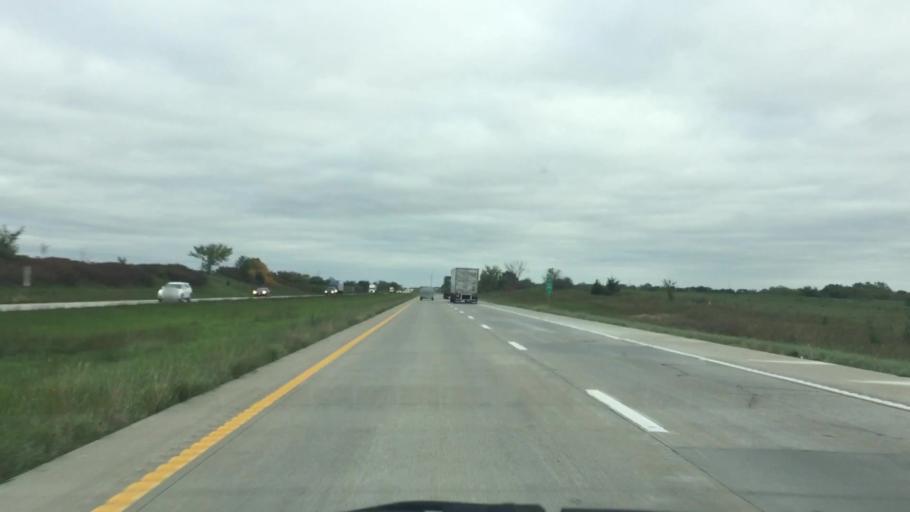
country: US
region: Missouri
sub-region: Clinton County
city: Lathrop
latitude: 39.6158
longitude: -94.2491
